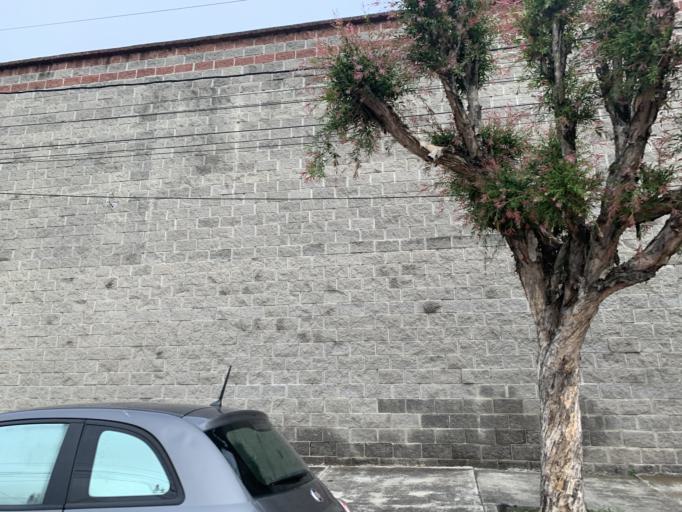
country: GT
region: Guatemala
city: Guatemala City
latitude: 14.6019
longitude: -90.5499
